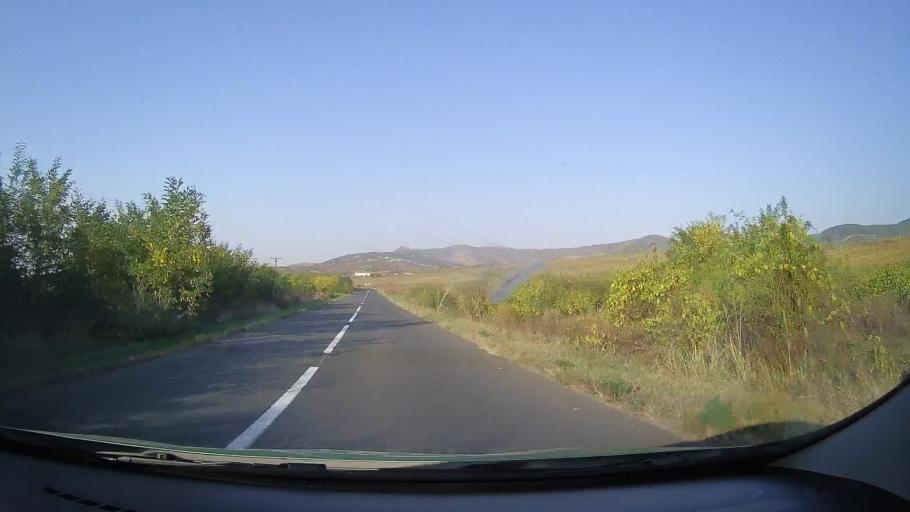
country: RO
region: Arad
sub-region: Comuna Siria
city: Siria
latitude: 46.2301
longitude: 21.6362
